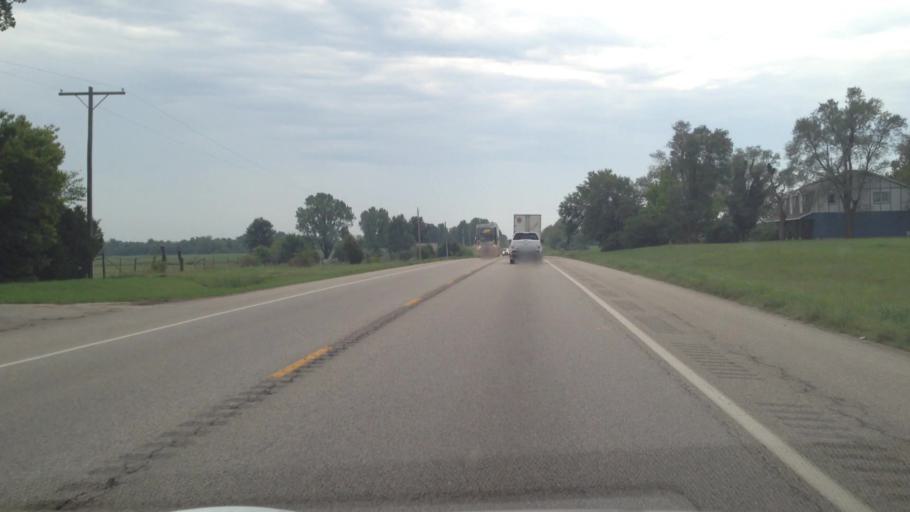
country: US
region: Kansas
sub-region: Crawford County
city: Pittsburg
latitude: 37.3274
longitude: -94.7055
